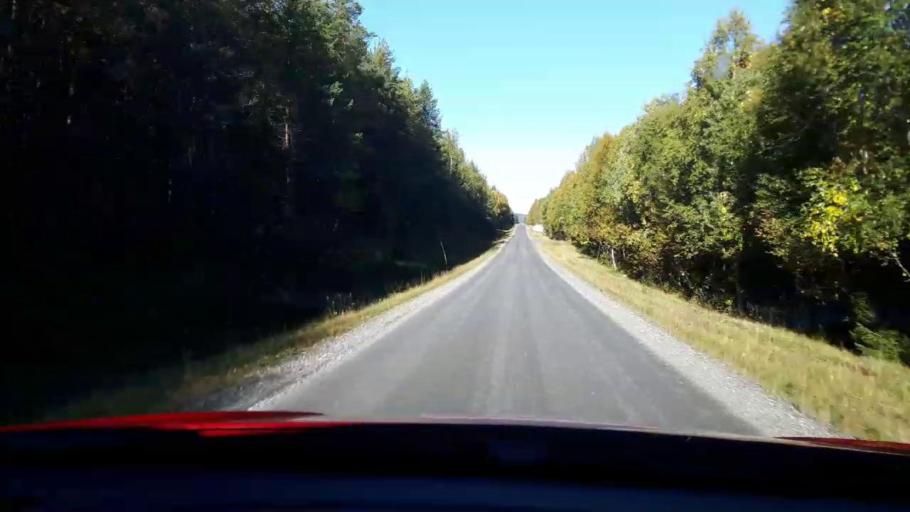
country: NO
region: Nord-Trondelag
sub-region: Lierne
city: Sandvika
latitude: 64.5399
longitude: 14.0035
